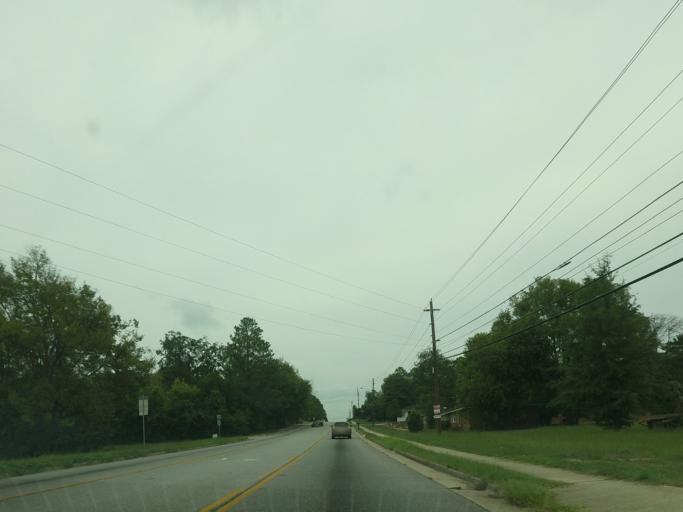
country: US
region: Georgia
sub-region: Bibb County
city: Macon
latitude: 32.8202
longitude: -83.6690
